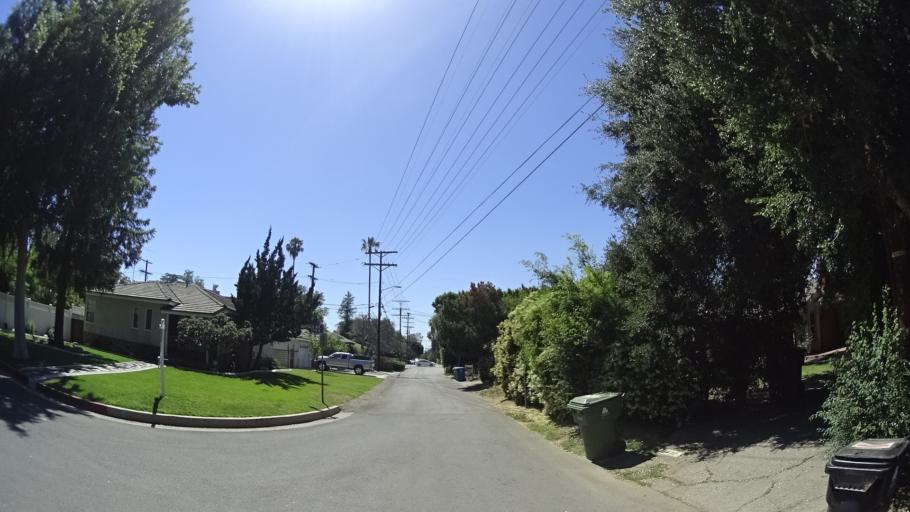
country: US
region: California
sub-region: Los Angeles County
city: Van Nuys
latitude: 34.1757
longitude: -118.4301
